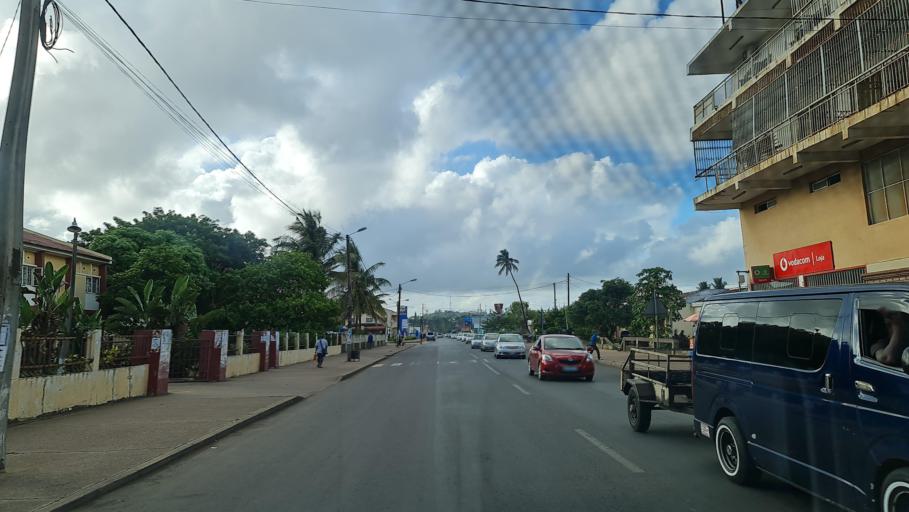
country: MZ
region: Gaza
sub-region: Xai-Xai District
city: Xai-Xai
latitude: -25.0468
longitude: 33.6446
